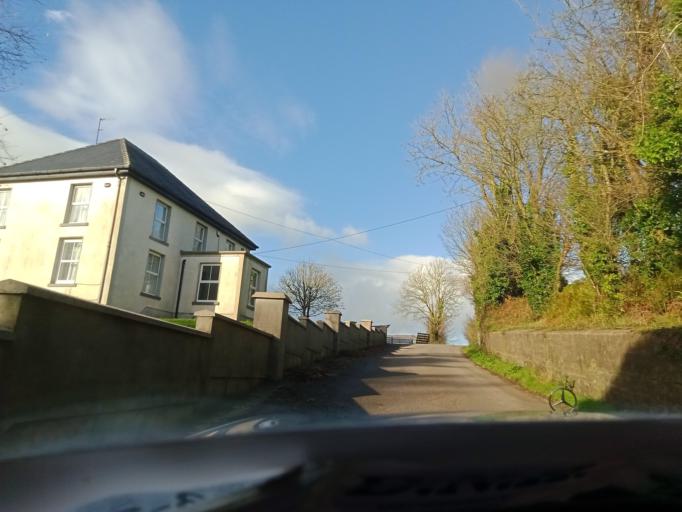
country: IE
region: Leinster
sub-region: Kilkenny
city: Mooncoin
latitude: 52.2764
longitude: -7.2462
